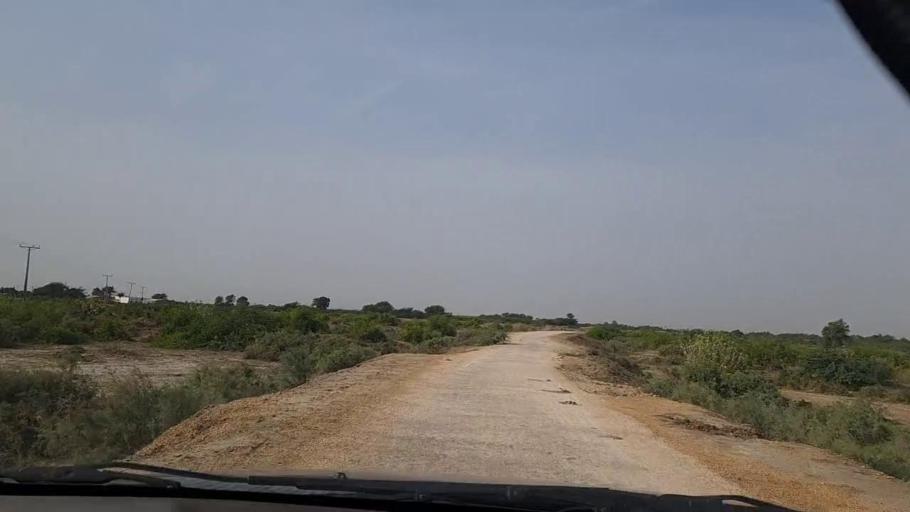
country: PK
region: Sindh
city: Thatta
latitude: 24.6084
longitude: 67.9548
